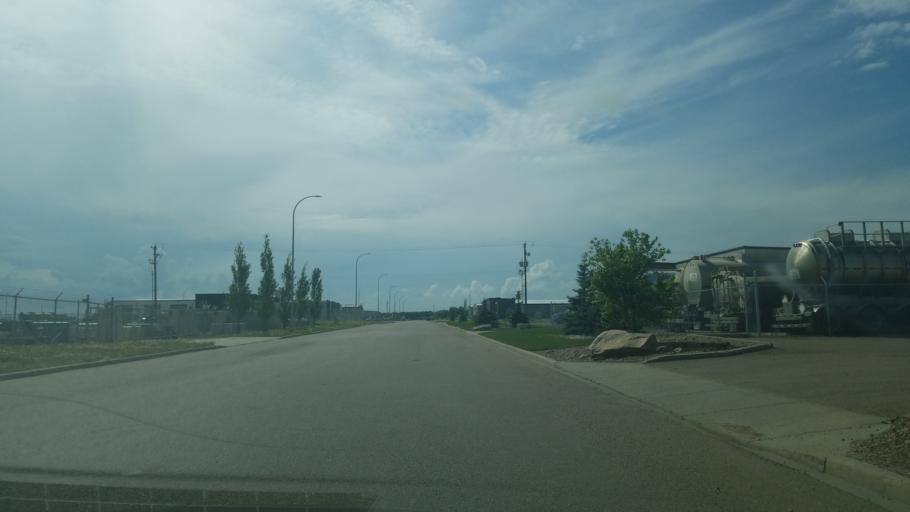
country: CA
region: Saskatchewan
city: Lloydminster
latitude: 53.2915
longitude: -110.0429
